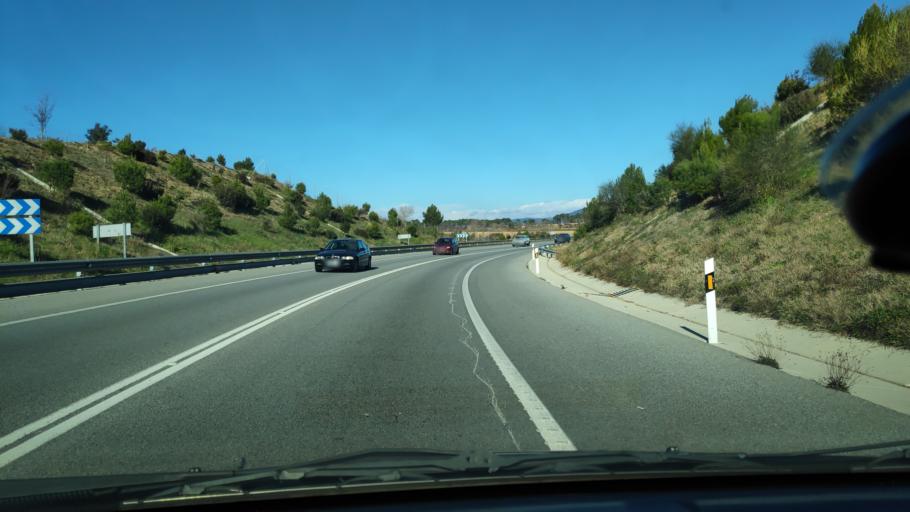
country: ES
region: Catalonia
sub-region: Provincia de Barcelona
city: Sant Quirze del Valles
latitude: 41.5694
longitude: 2.0759
